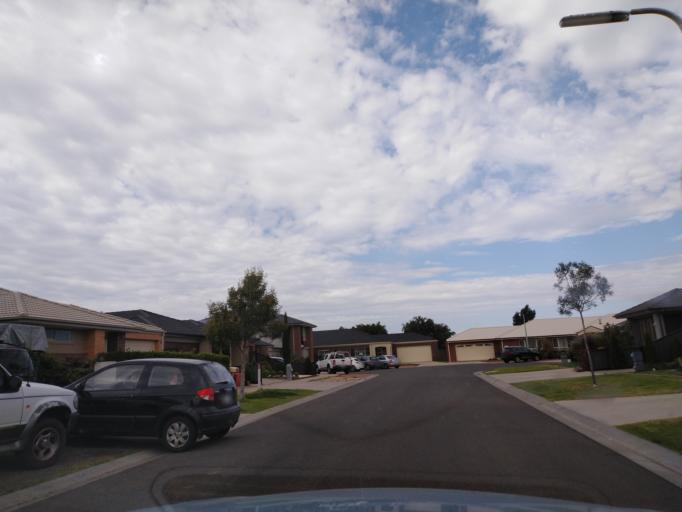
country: AU
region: Victoria
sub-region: Wyndham
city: Williams Landing
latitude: -37.8450
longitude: 144.7153
